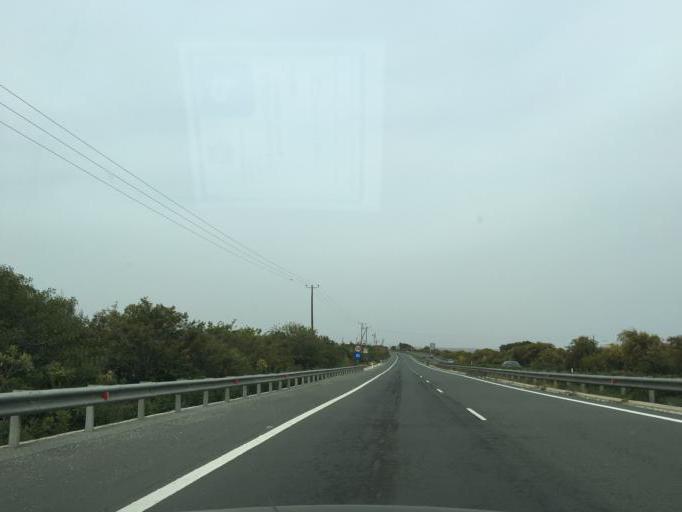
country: CY
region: Ammochostos
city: Liopetri
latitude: 34.9872
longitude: 33.9363
